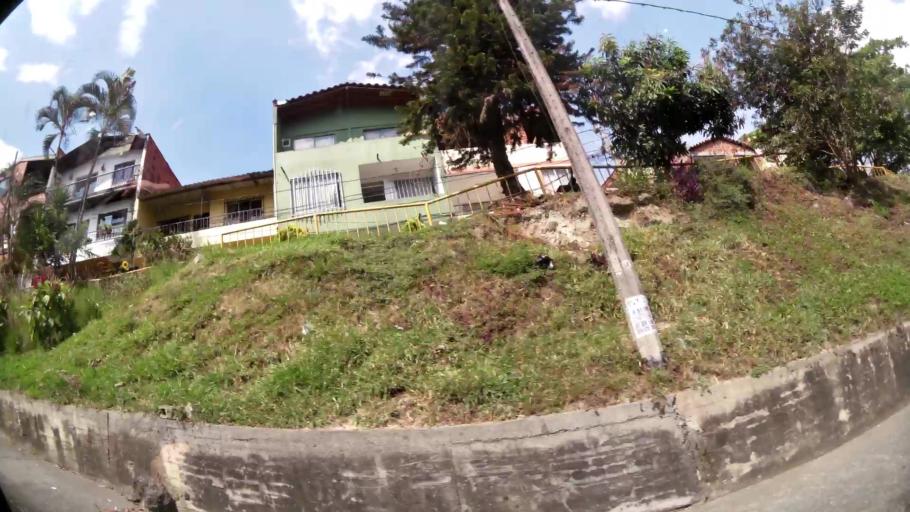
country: CO
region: Antioquia
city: Medellin
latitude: 6.2882
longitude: -75.5898
